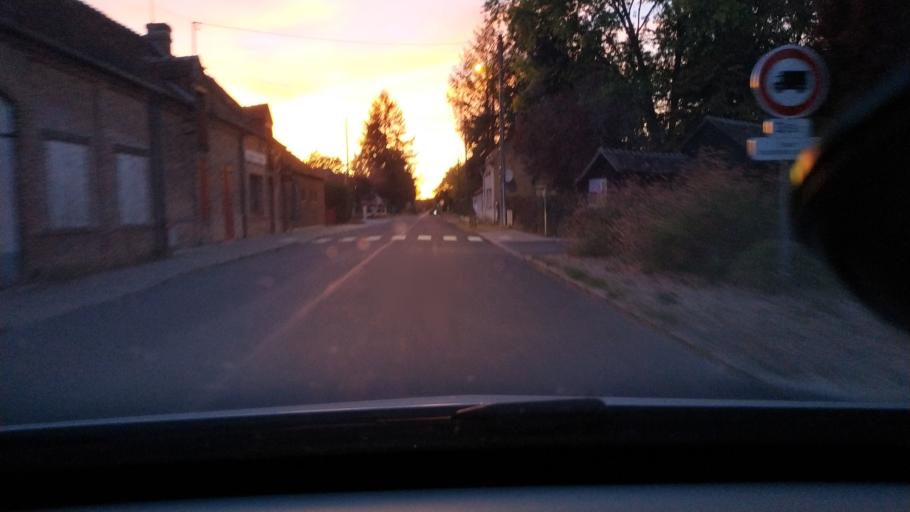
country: FR
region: Centre
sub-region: Departement du Cher
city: Brinon-sur-Sauldre
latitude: 47.6087
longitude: 2.1723
